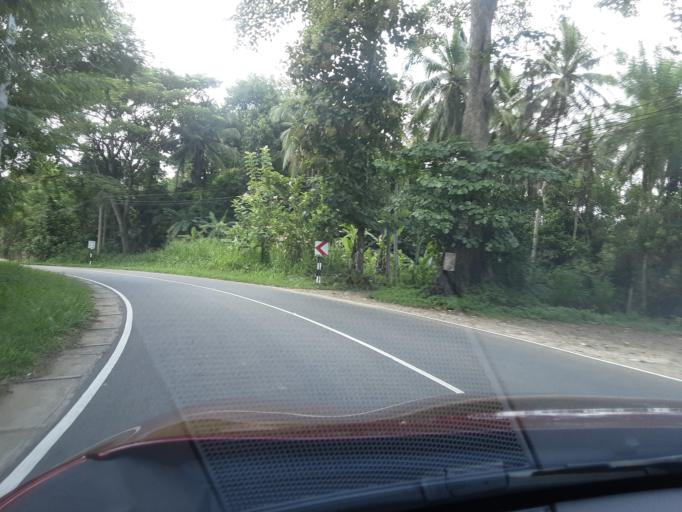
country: LK
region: Uva
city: Monaragala
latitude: 6.8946
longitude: 81.2909
